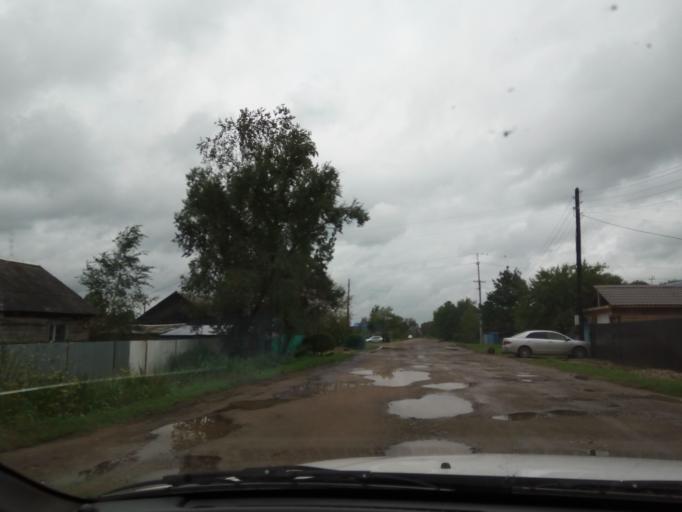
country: RU
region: Primorskiy
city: Dal'nerechensk
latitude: 45.9171
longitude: 133.7237
